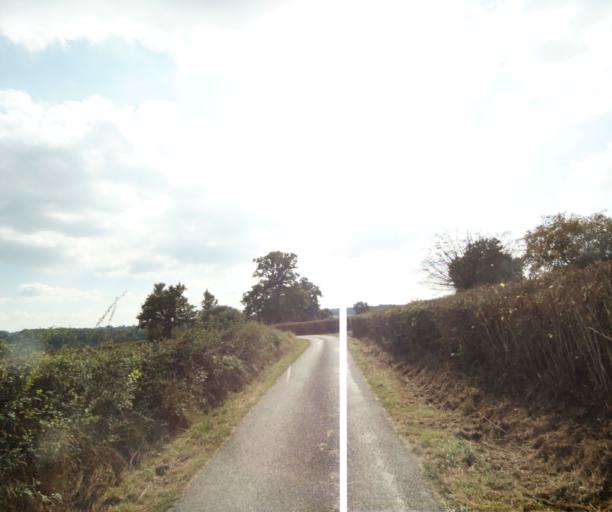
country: FR
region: Bourgogne
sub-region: Departement de Saone-et-Loire
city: Palinges
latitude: 46.4957
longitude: 4.2348
